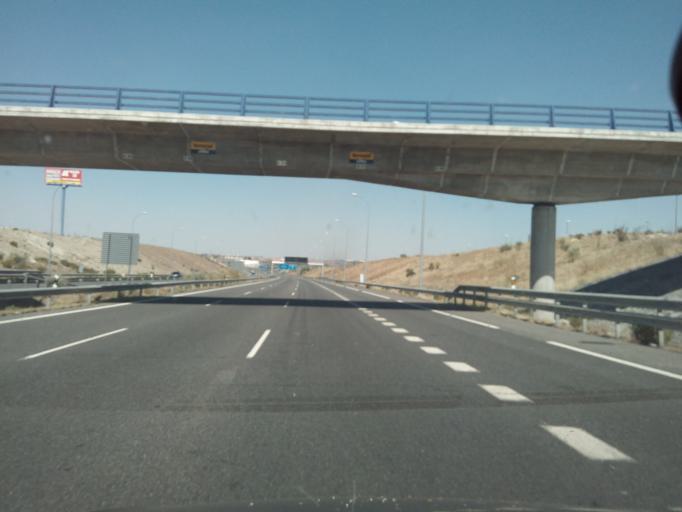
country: ES
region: Madrid
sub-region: Provincia de Madrid
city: Villa de Vallecas
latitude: 40.3483
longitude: -3.5818
